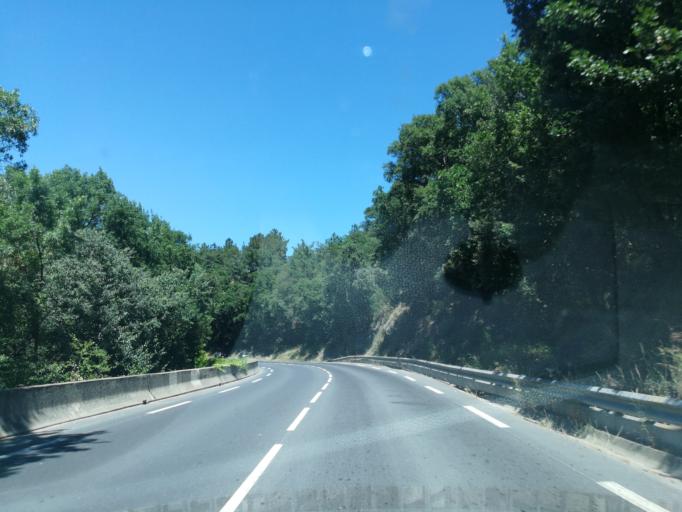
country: FR
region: Languedoc-Roussillon
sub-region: Departement des Pyrenees-Orientales
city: Maureillas-las-Illas
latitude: 42.5030
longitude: 2.8239
